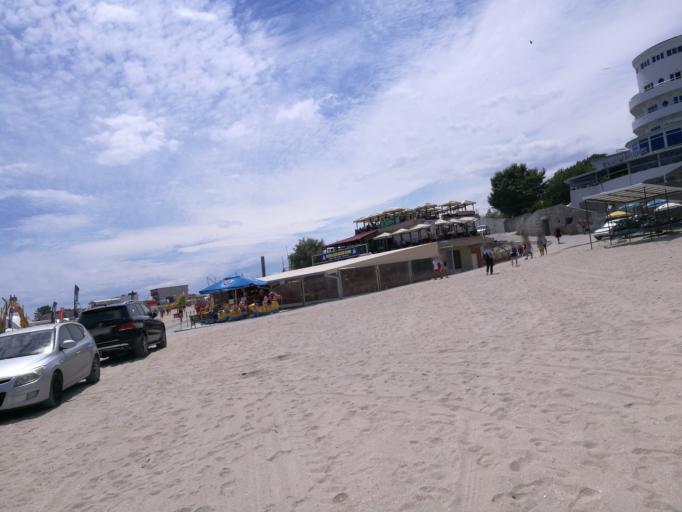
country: RO
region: Constanta
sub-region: Oras Eforie
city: Eforie Nord
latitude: 44.0633
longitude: 28.6403
